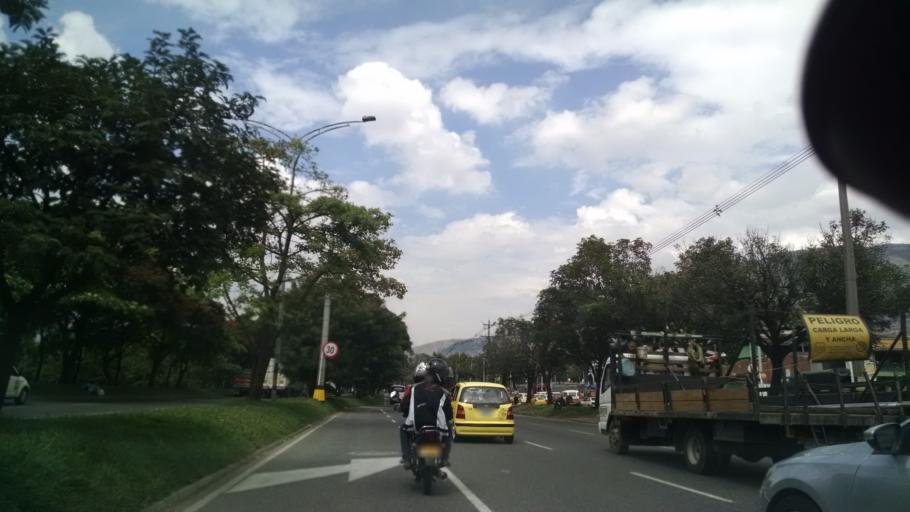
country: CO
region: Antioquia
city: Medellin
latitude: 6.2573
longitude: -75.5750
